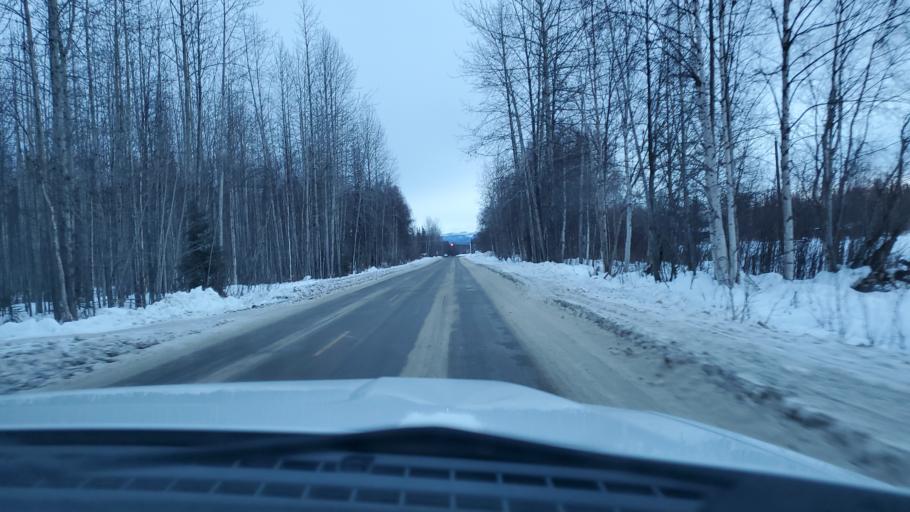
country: US
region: Alaska
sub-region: Matanuska-Susitna Borough
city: Y
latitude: 62.3163
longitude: -150.2408
